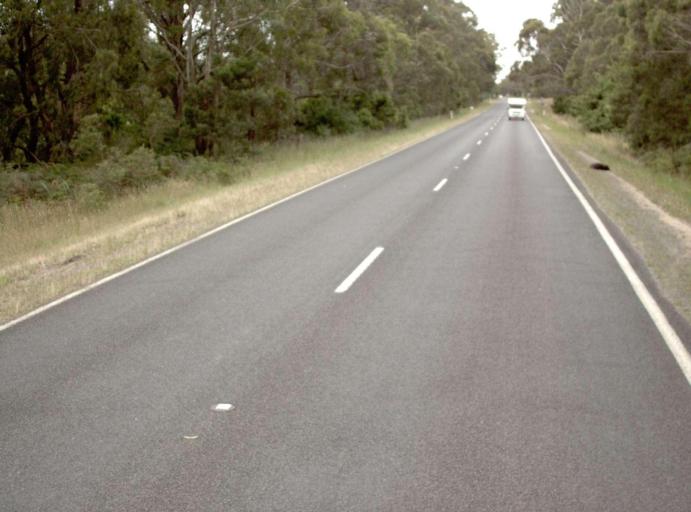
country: AU
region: Victoria
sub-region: Wellington
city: Sale
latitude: -38.5290
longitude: 146.8653
